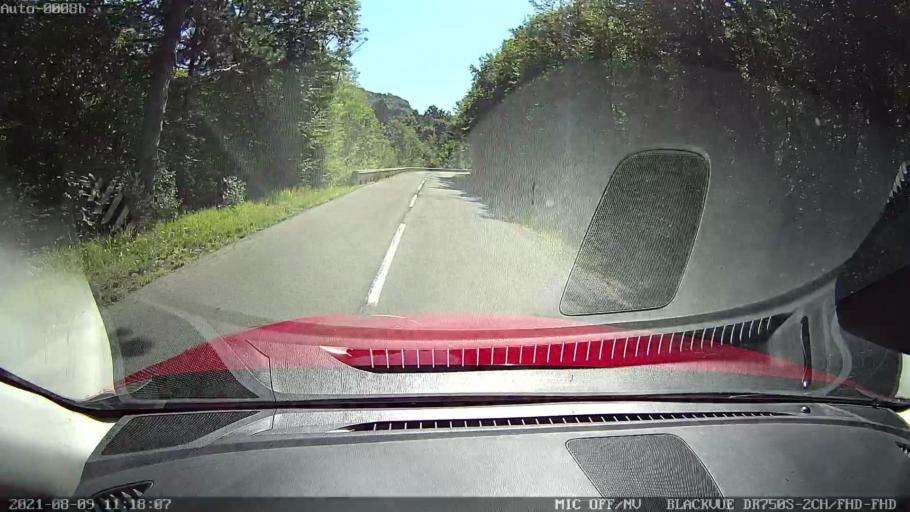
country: HR
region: Istarska
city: Lovran
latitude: 45.3105
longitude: 14.1922
